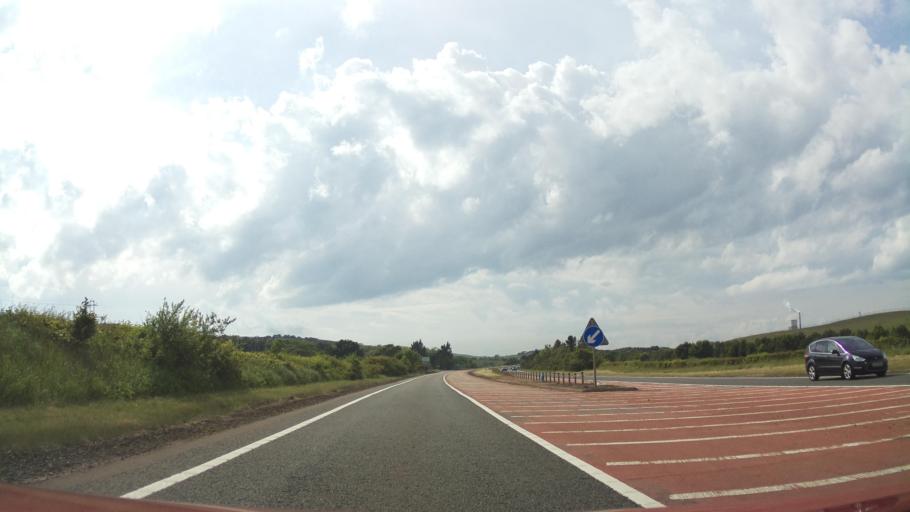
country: GB
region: Scotland
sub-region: East Lothian
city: Dunbar
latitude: 55.9663
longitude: -2.4470
